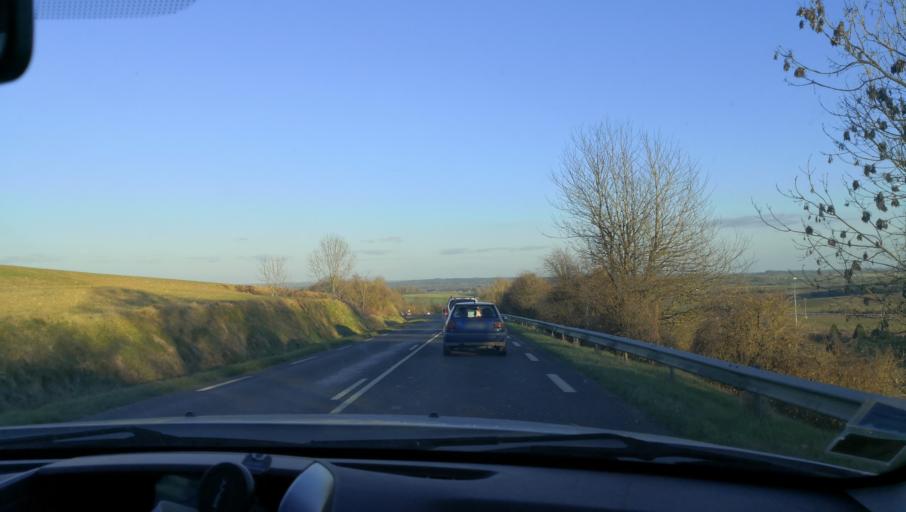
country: FR
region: Haute-Normandie
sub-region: Departement de la Seine-Maritime
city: Buchy
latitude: 49.5934
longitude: 1.4477
